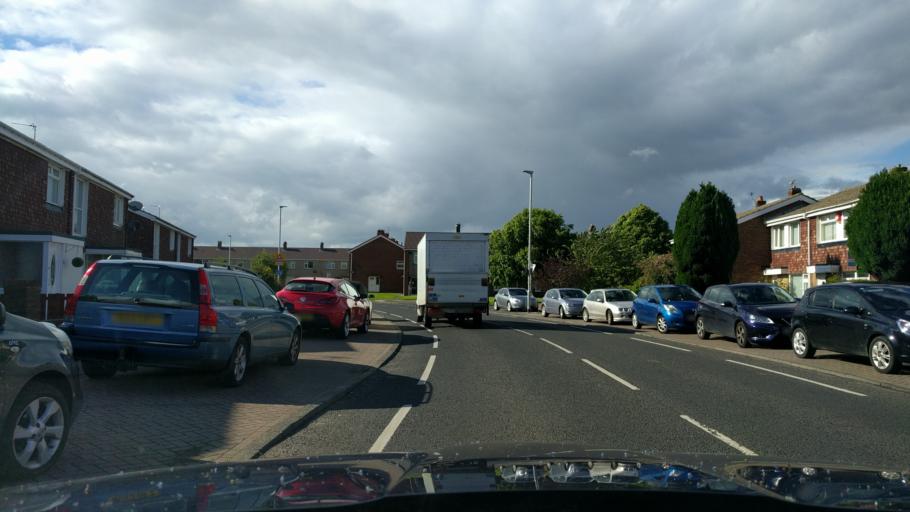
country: GB
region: England
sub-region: Northumberland
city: Ashington
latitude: 55.1709
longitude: -1.5526
